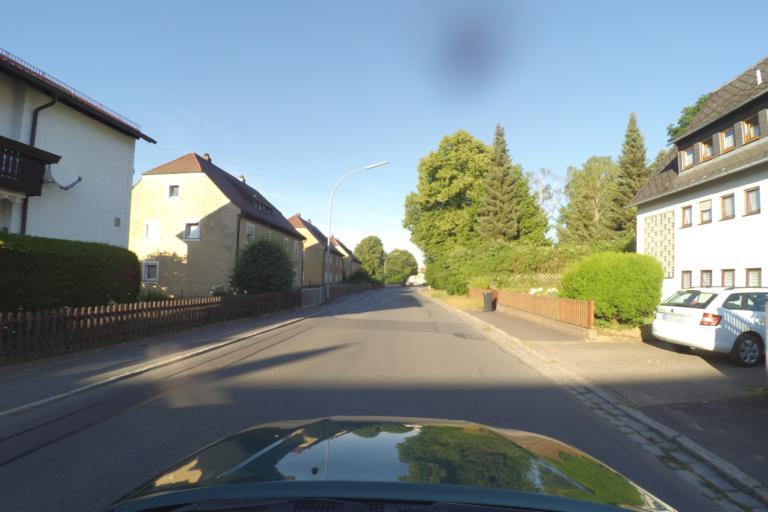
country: DE
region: Bavaria
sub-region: Upper Palatinate
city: Kemnath
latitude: 49.8677
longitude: 11.8941
